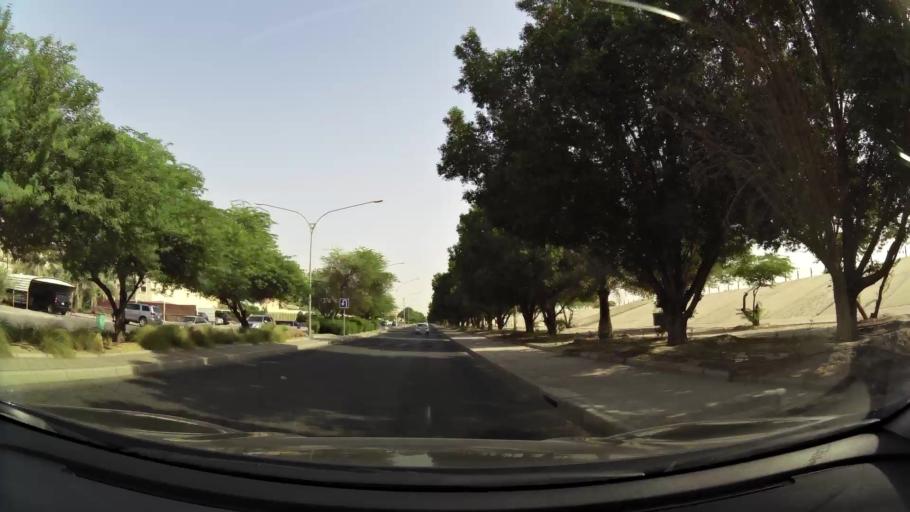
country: KW
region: Muhafazat al Jahra'
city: Al Jahra'
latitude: 29.3206
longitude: 47.6638
